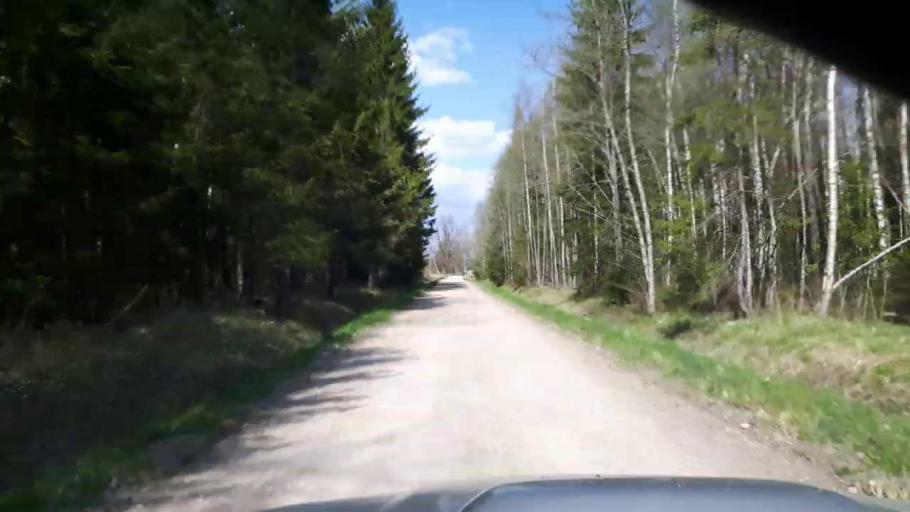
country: EE
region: Paernumaa
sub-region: Tootsi vald
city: Tootsi
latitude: 58.4564
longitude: 24.8869
